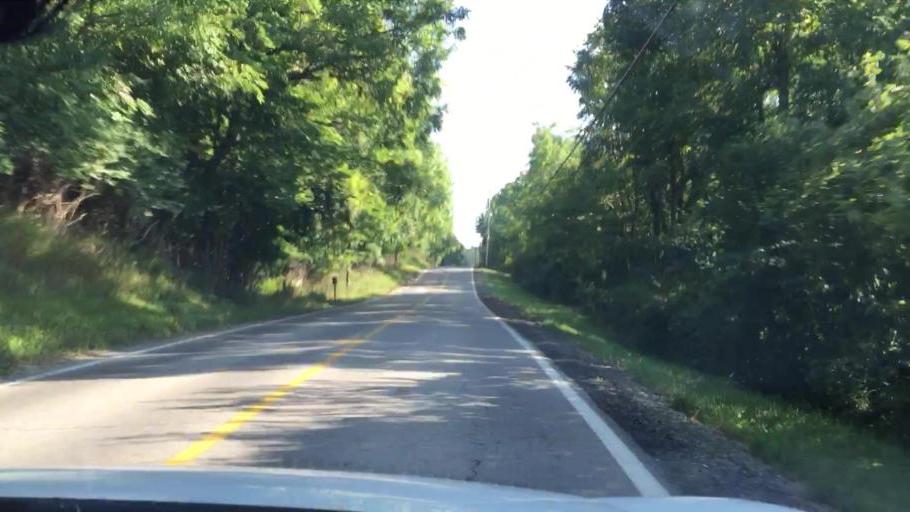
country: US
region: Ohio
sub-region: Clark County
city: Northridge
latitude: 39.9869
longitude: -83.7053
